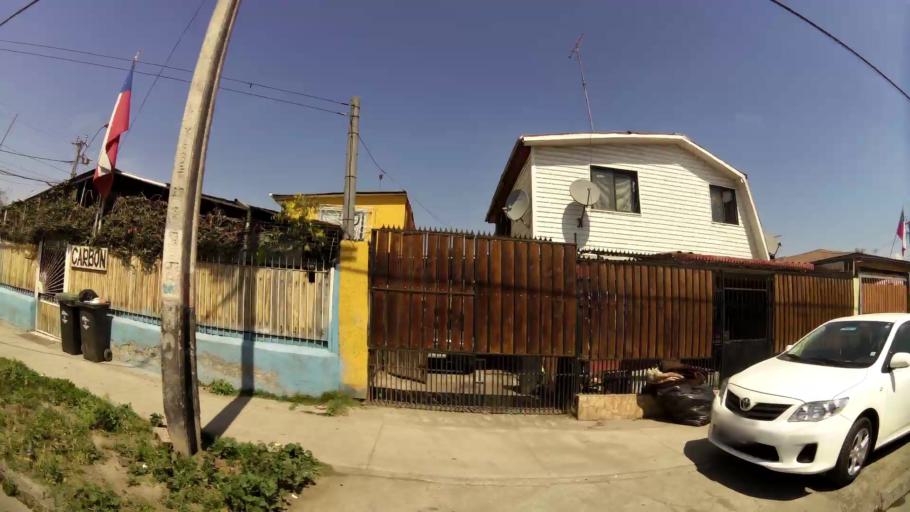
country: CL
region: Santiago Metropolitan
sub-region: Provincia de Santiago
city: La Pintana
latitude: -33.5467
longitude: -70.6397
